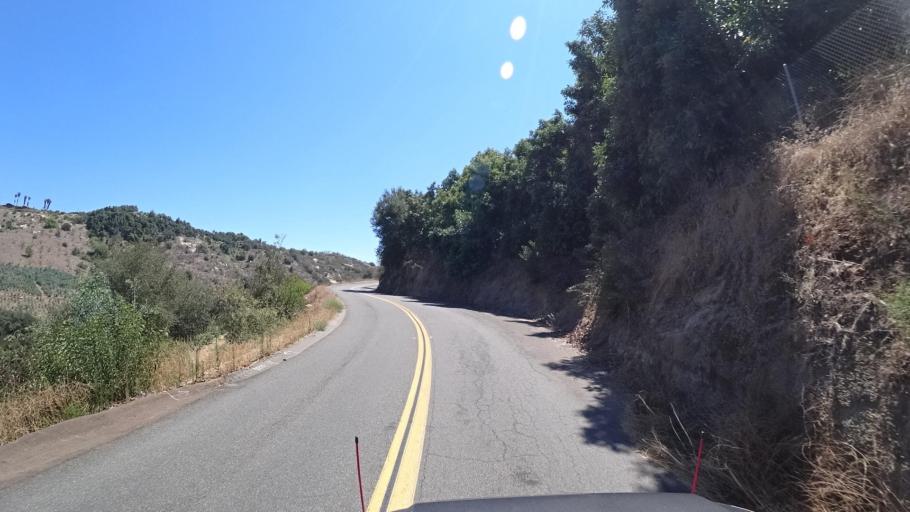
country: US
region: California
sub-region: San Diego County
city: Hidden Meadows
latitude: 33.3119
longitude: -117.0974
